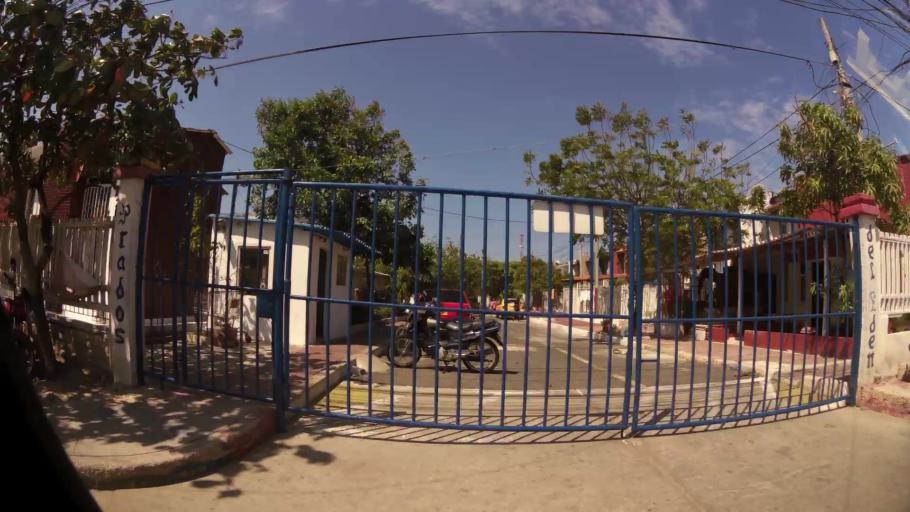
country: CO
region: Atlantico
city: Barranquilla
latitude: 10.9755
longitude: -74.8338
